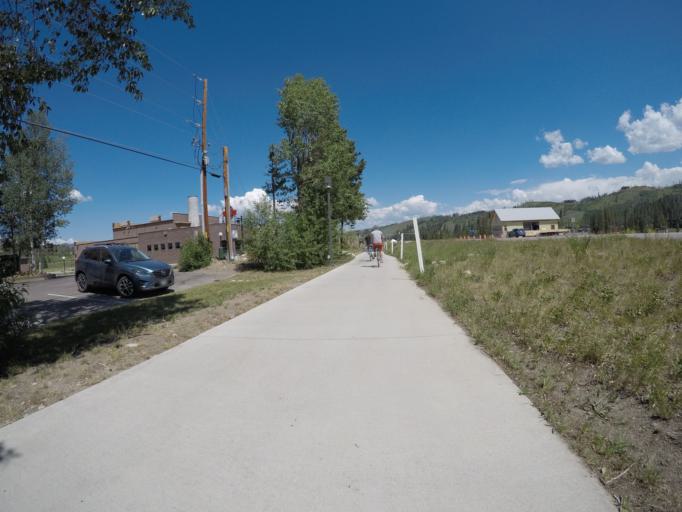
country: US
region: Colorado
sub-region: Grand County
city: Fraser
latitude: 39.9275
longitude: -105.7886
